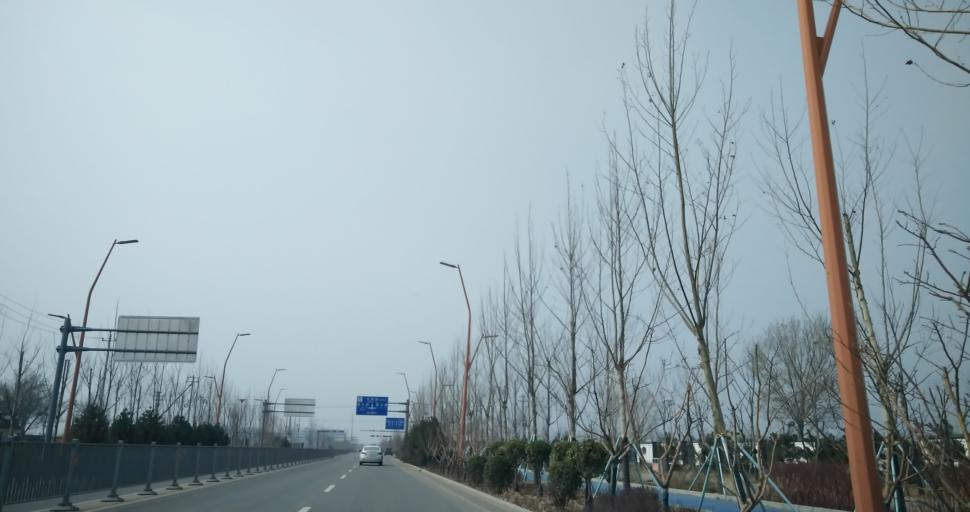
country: CN
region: Beijing
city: Weishanzhuang
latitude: 39.6840
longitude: 116.4102
